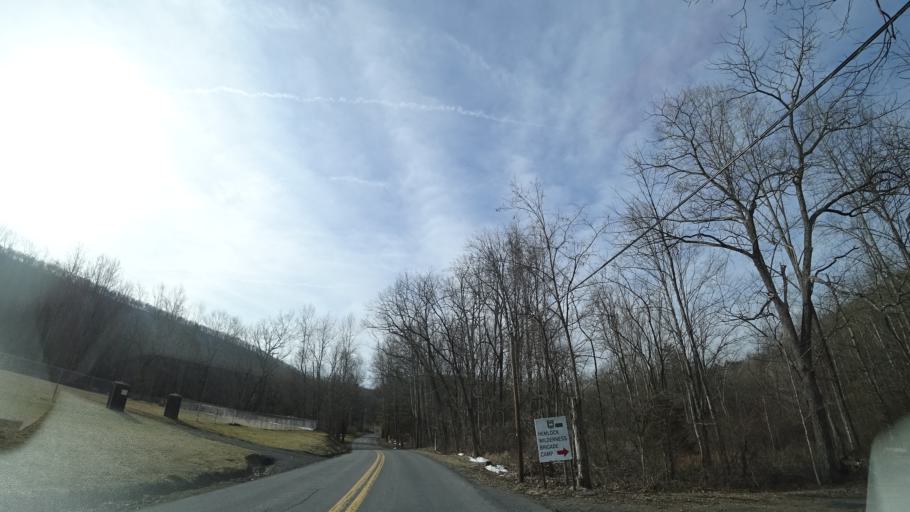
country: US
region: Virginia
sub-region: Shenandoah County
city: Woodstock
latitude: 39.0488
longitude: -78.6357
